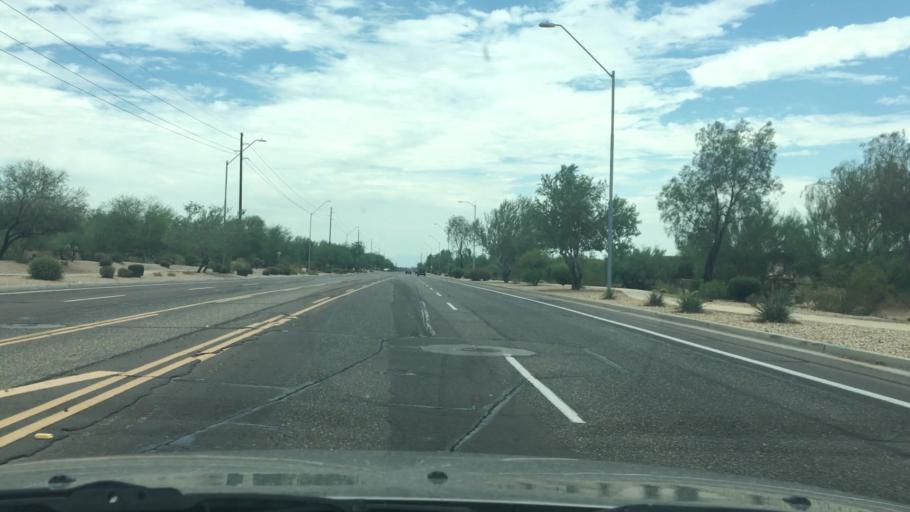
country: US
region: Arizona
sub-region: Maricopa County
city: Sun City
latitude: 33.7228
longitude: -112.2033
